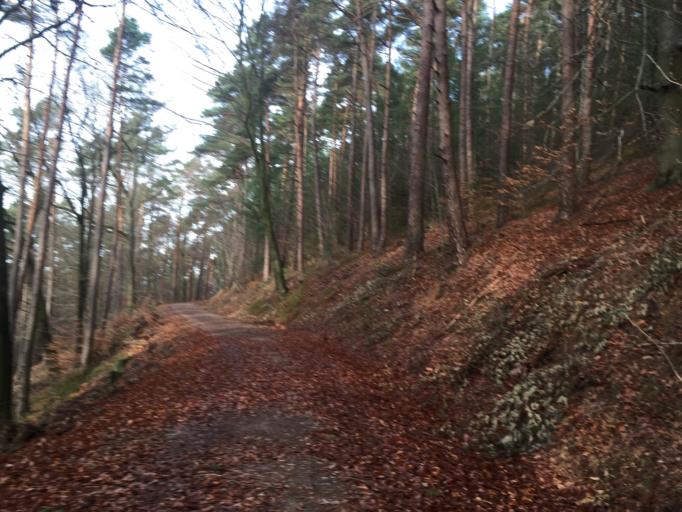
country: DE
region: Hesse
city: Reichelsheim
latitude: 49.6961
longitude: 8.8940
